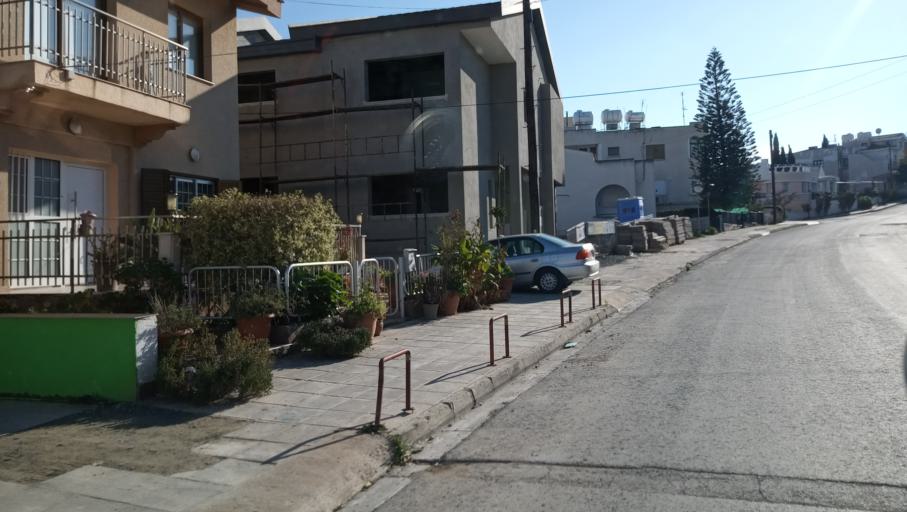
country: CY
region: Lefkosia
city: Nicosia
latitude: 35.1392
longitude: 33.3156
